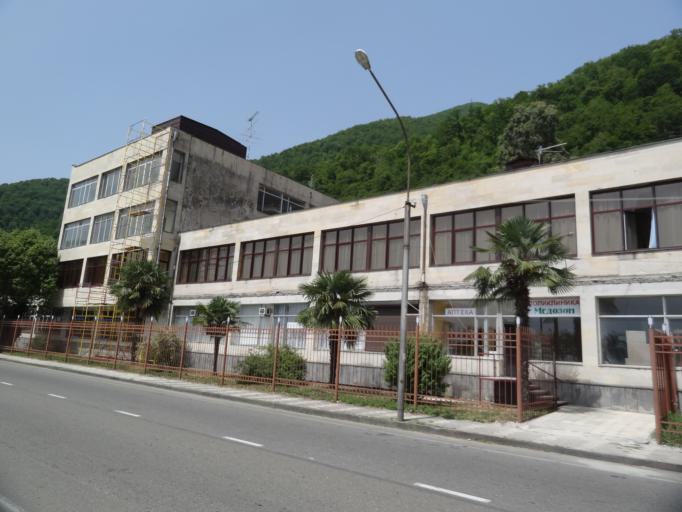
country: GE
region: Abkhazia
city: Gagra
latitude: 43.3199
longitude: 40.2399
